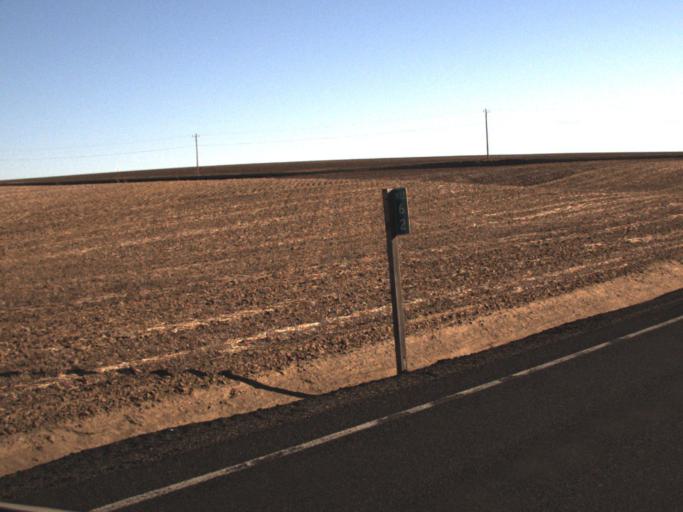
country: US
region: Washington
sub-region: Adams County
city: Ritzville
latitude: 47.1048
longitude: -118.3655
